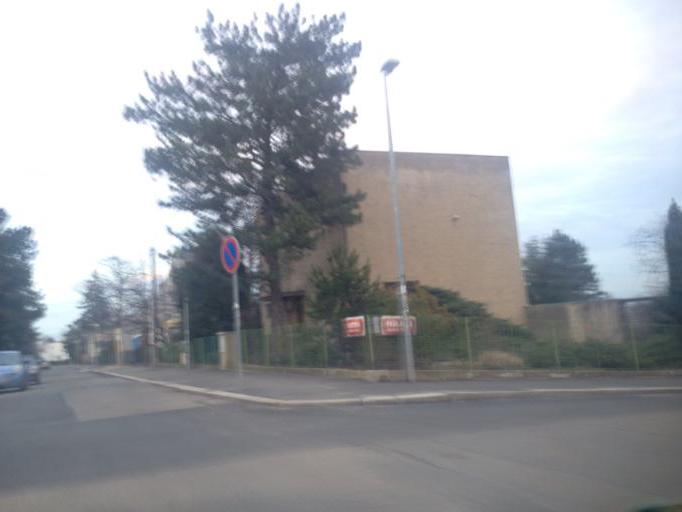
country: CZ
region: Praha
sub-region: Praha 1
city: Mala Strana
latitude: 50.1148
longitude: 14.3843
